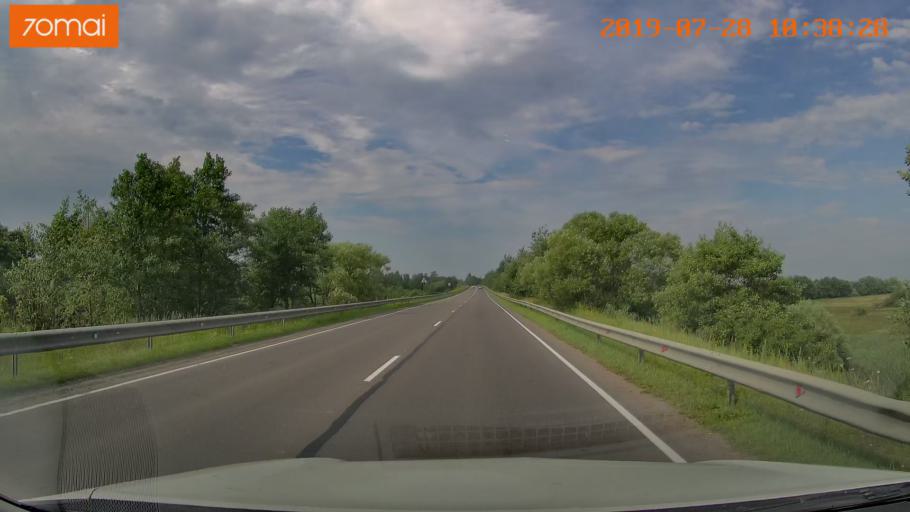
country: RU
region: Kaliningrad
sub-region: Gorod Kaliningrad
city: Kaliningrad
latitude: 54.7238
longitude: 20.3984
